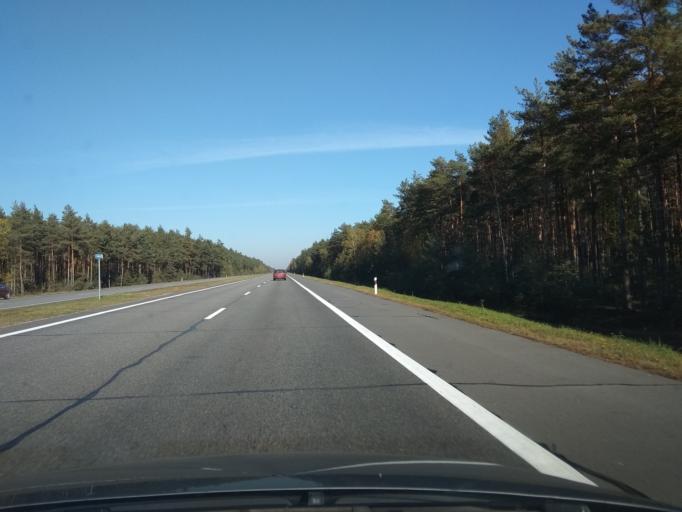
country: BY
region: Grodnenskaya
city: Zhyrovichy
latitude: 52.9324
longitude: 25.6987
